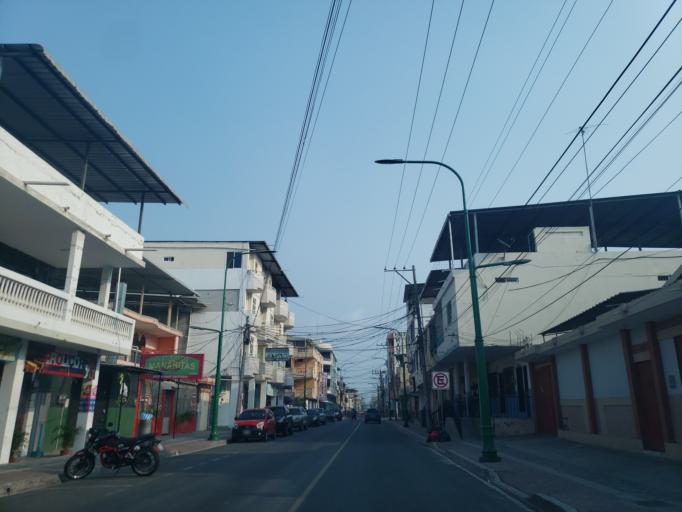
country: EC
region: Manabi
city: Manta
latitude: -0.9468
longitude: -80.7334
